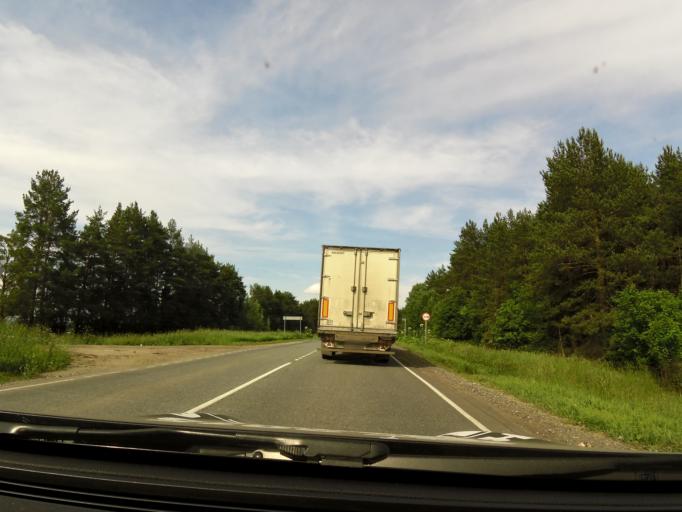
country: RU
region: Kirov
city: Slobodskoy
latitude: 58.7547
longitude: 50.3243
